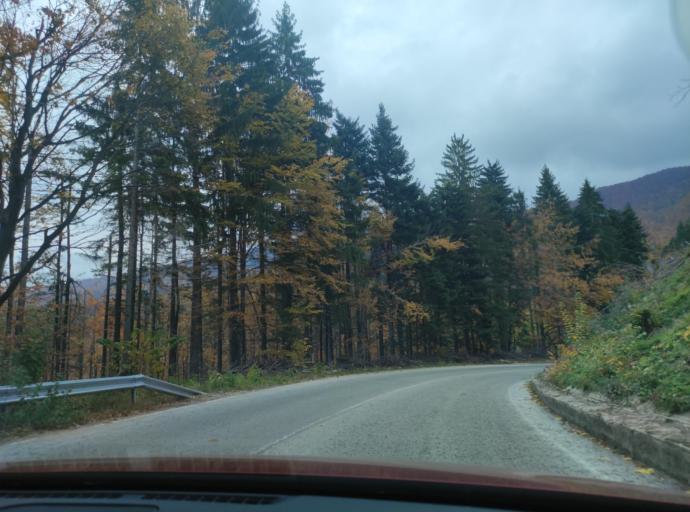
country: BG
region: Montana
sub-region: Obshtina Berkovitsa
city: Berkovitsa
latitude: 43.1475
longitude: 23.1495
